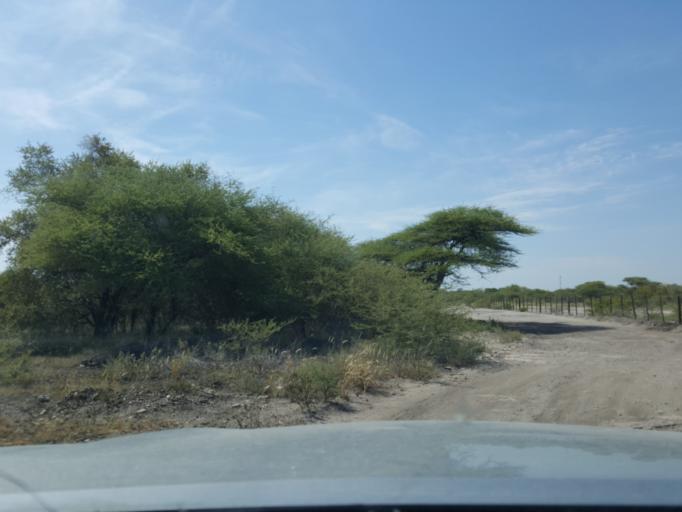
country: BW
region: North West
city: Shakawe
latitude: -18.7802
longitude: 21.7368
